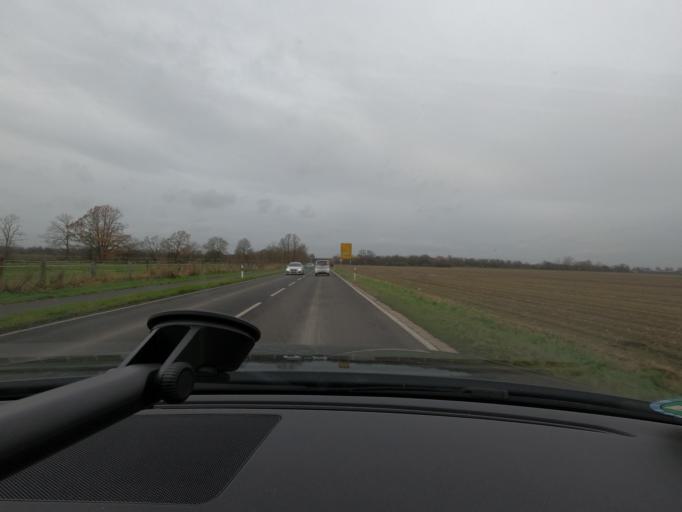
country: DE
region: North Rhine-Westphalia
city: Kempen
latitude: 51.3565
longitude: 6.4461
